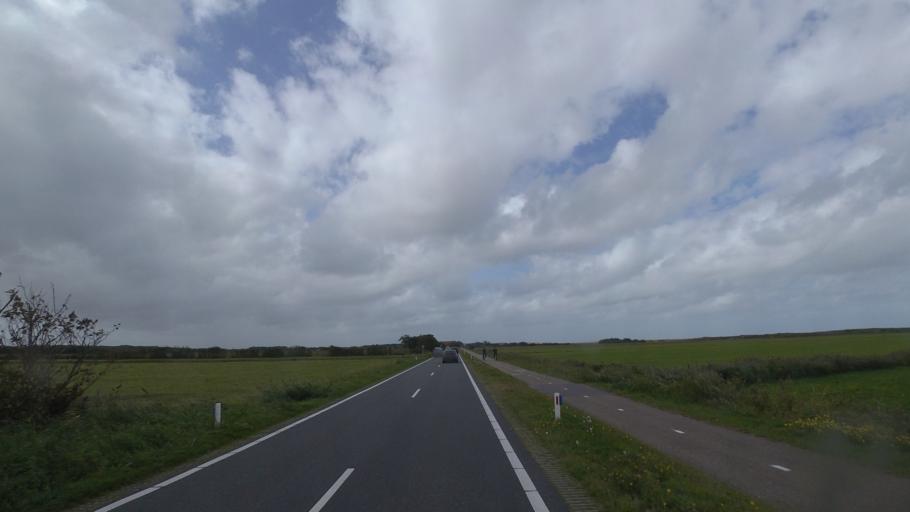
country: NL
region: Friesland
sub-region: Gemeente Ameland
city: Hollum
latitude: 53.4463
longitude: 5.6771
